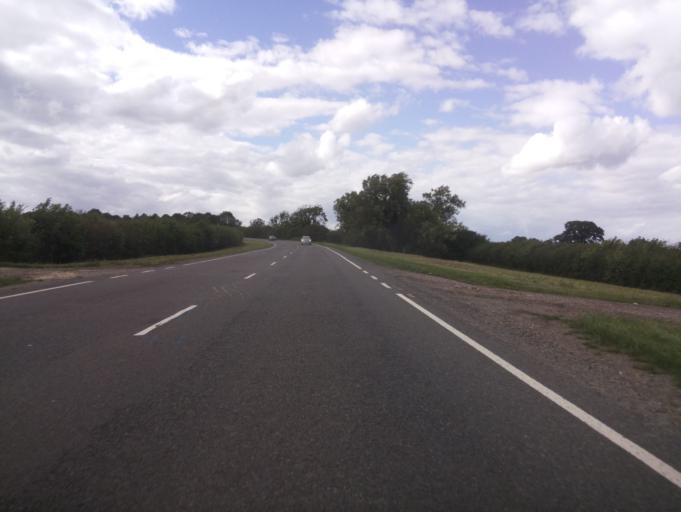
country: GB
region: England
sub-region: Leicestershire
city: Measham
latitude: 52.6360
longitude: -1.4940
